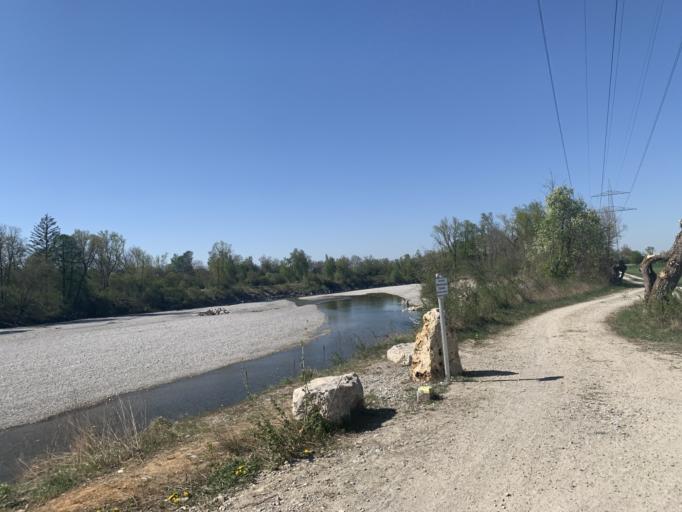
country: DE
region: Bavaria
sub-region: Swabia
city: Gersthofen
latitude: 48.4593
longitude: 10.8852
